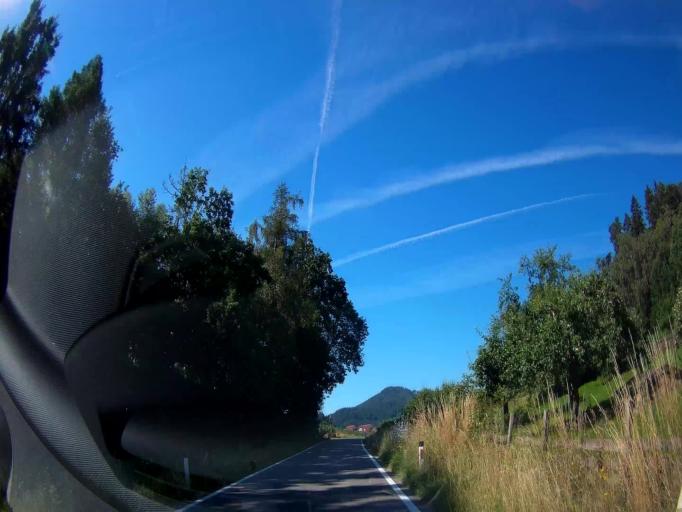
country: AT
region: Carinthia
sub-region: Politischer Bezirk Klagenfurt Land
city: Maria Saal
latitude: 46.6878
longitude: 14.3579
